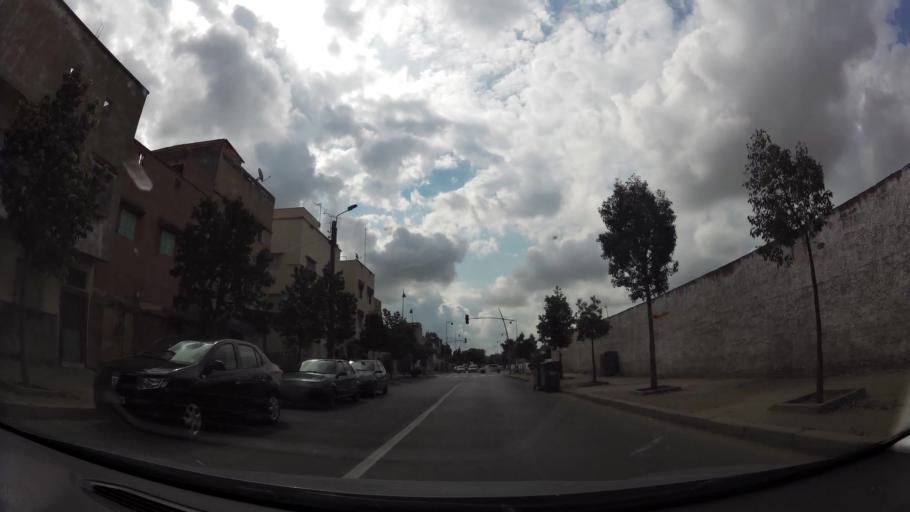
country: MA
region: Gharb-Chrarda-Beni Hssen
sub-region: Kenitra Province
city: Kenitra
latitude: 34.2595
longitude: -6.5657
